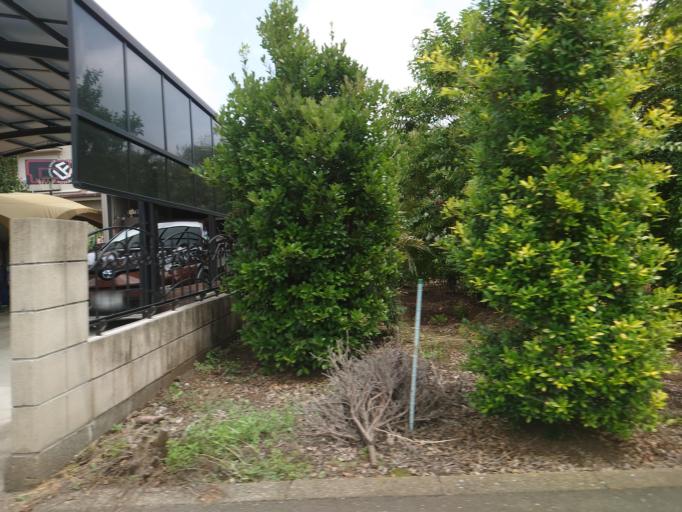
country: JP
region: Saitama
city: Hanno
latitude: 35.7959
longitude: 139.3023
